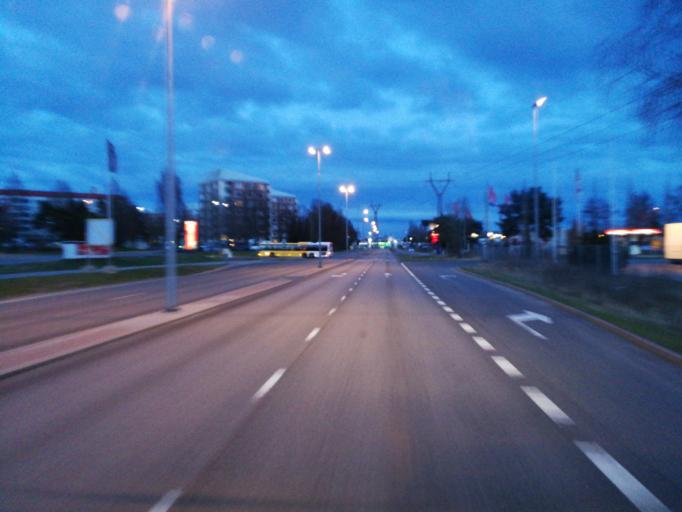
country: FI
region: Varsinais-Suomi
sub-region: Turku
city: Turku
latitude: 60.4469
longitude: 22.2198
